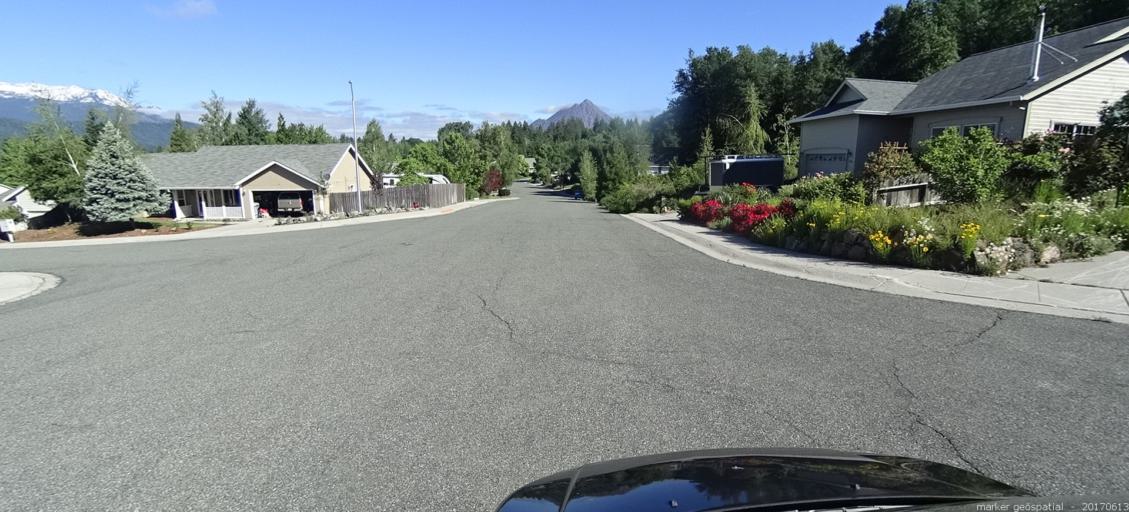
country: US
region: California
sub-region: Siskiyou County
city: Mount Shasta
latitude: 41.3020
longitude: -122.3023
